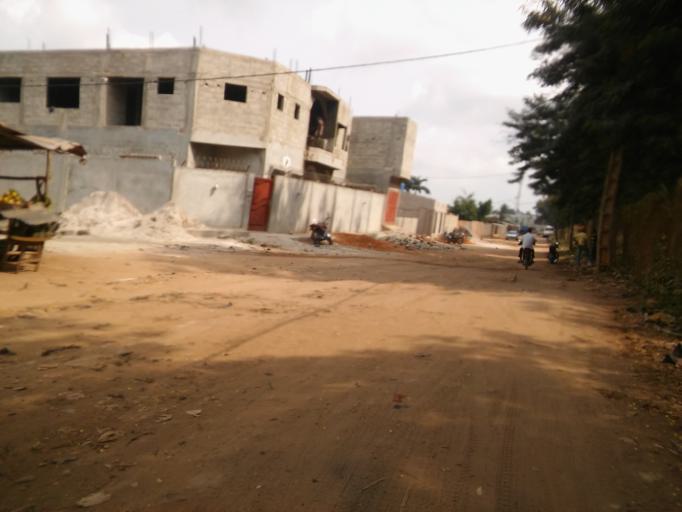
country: BJ
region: Atlantique
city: Abomey-Calavi
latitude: 6.4211
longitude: 2.3247
